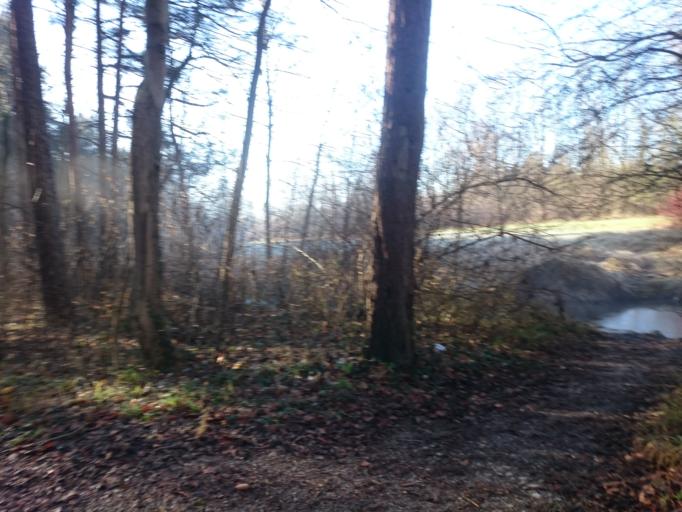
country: DE
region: Bavaria
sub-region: Swabia
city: Konigsbrunn
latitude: 48.3001
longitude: 10.9110
